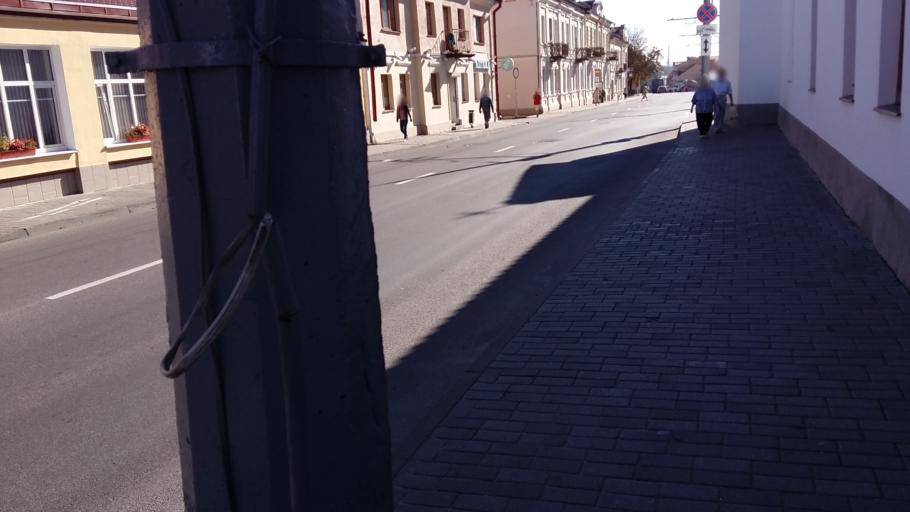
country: BY
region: Grodnenskaya
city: Hrodna
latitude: 53.6771
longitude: 23.8370
